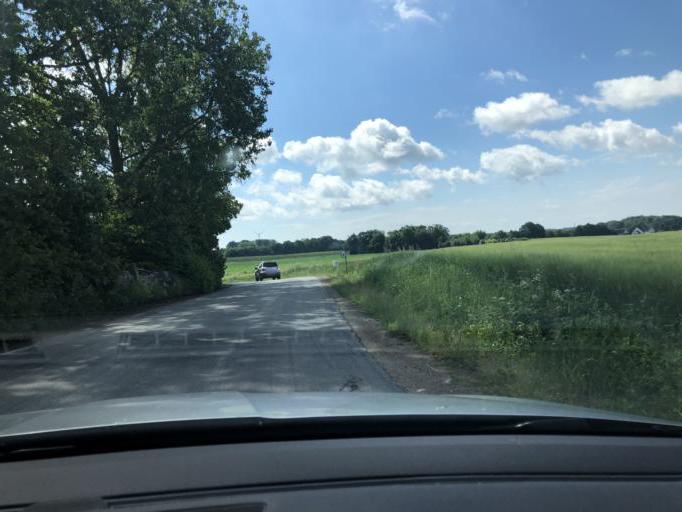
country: SE
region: Blekinge
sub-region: Solvesborgs Kommun
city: Soelvesborg
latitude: 56.0737
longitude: 14.6185
